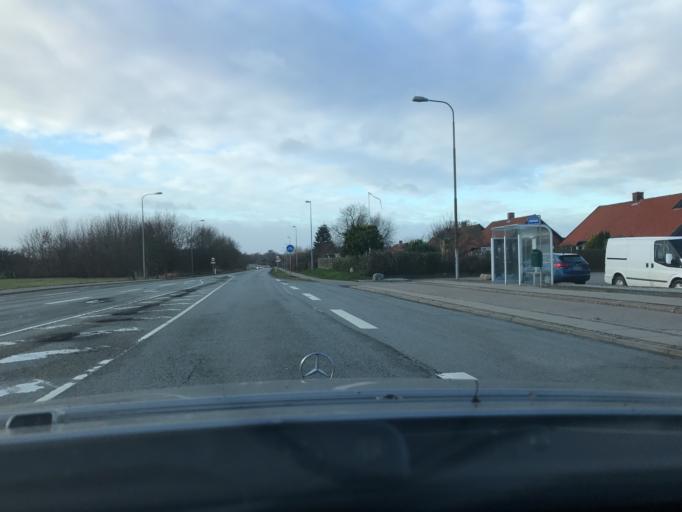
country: DK
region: South Denmark
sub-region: Sonderborg Kommune
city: Nordborg
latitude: 55.0491
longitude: 9.7772
